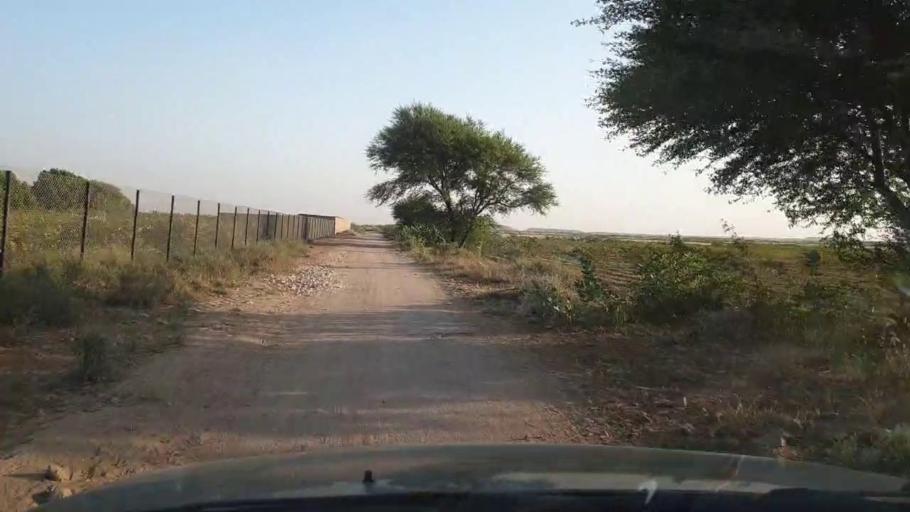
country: PK
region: Sindh
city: Kotri
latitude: 25.2227
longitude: 68.2267
